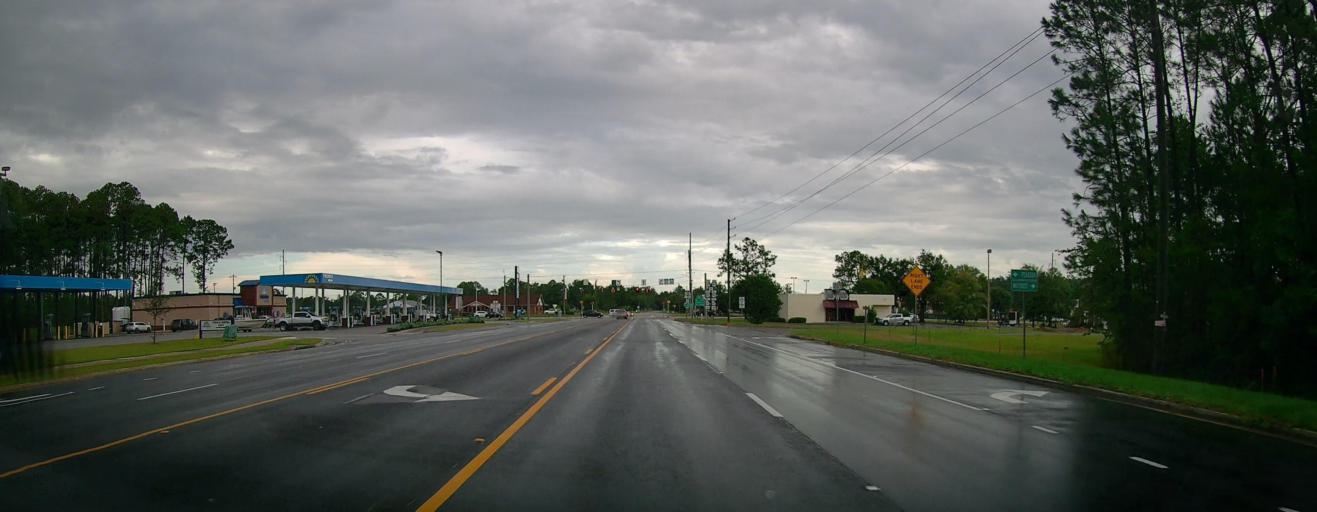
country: US
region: Georgia
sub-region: Ware County
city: Deenwood
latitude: 31.2071
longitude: -82.3838
